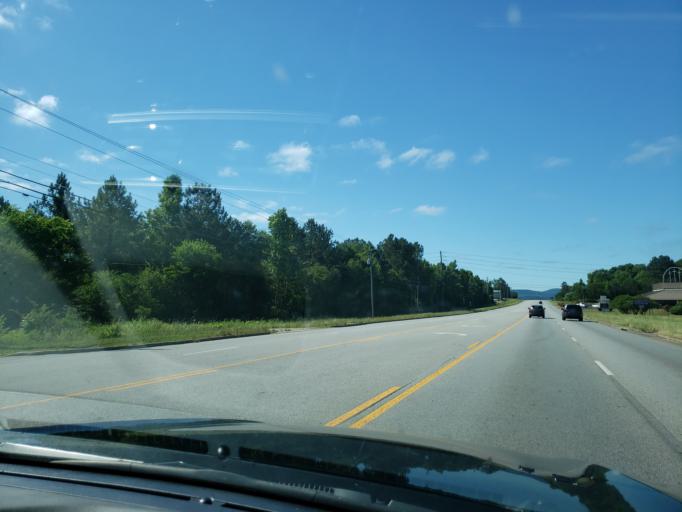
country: US
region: Alabama
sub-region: Calhoun County
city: Oxford
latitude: 33.6268
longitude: -85.7862
